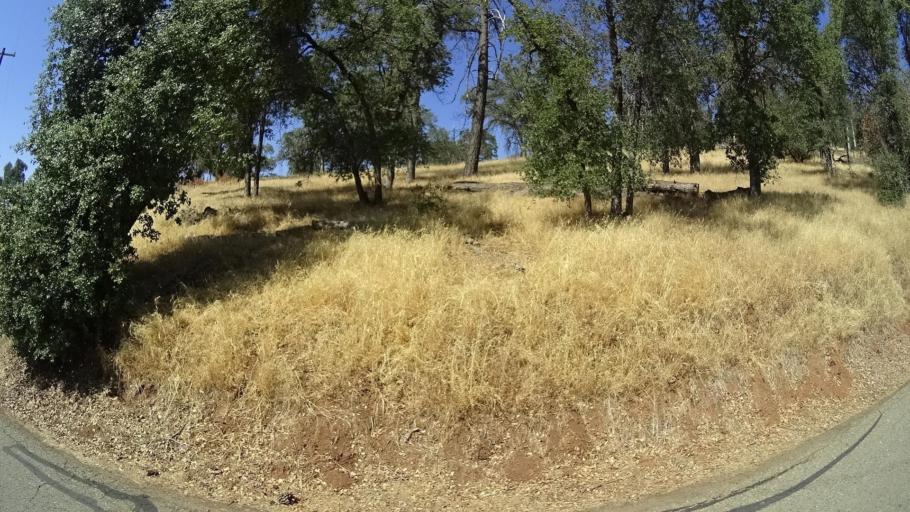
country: US
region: California
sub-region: Mariposa County
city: Mariposa
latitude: 37.4697
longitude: -119.9190
